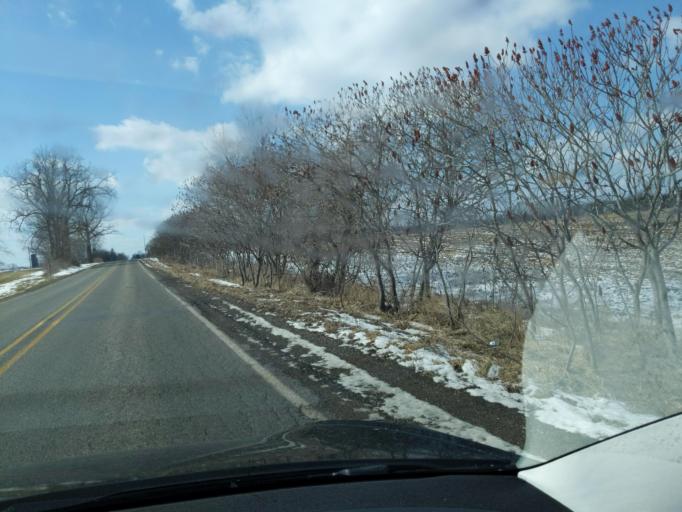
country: US
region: Michigan
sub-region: Livingston County
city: Fowlerville
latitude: 42.6430
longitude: -84.0866
